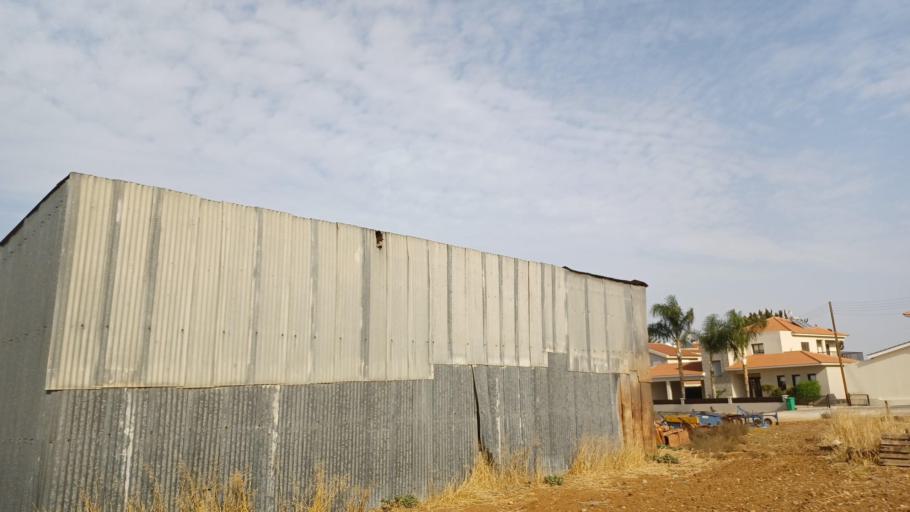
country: CY
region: Lefkosia
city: Peristerona
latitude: 35.1273
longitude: 33.0872
